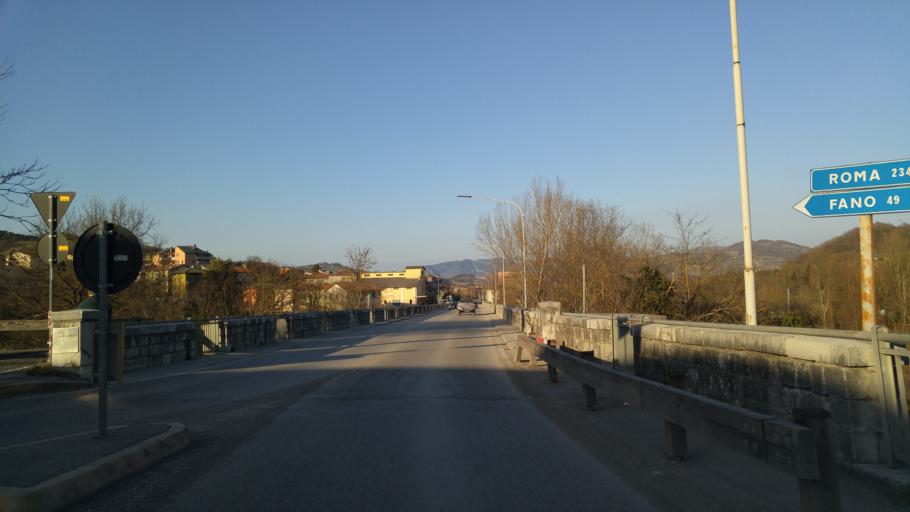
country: IT
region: The Marches
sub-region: Provincia di Pesaro e Urbino
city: Cagli
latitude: 43.5498
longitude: 12.6506
